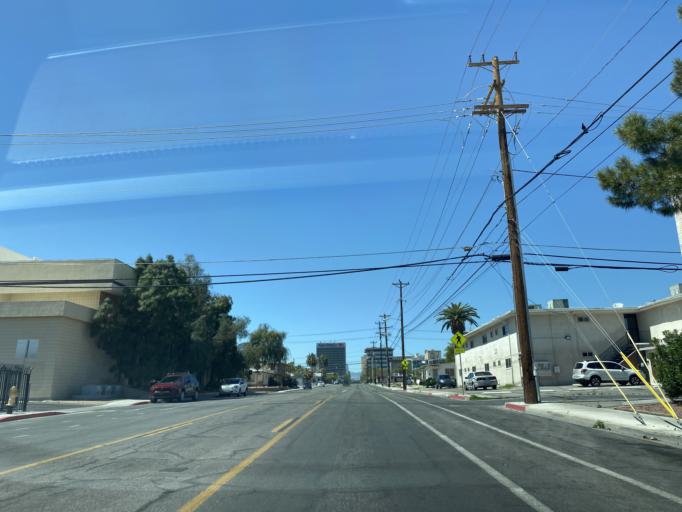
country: US
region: Nevada
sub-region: Clark County
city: Las Vegas
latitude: 36.1637
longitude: -115.1344
